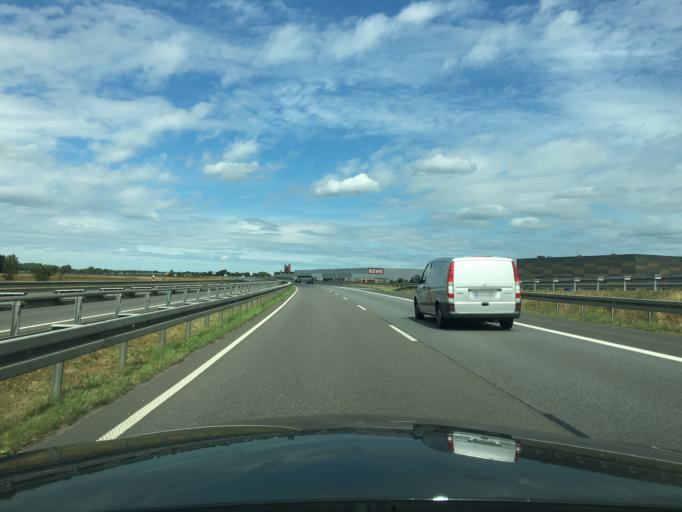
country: DE
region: Brandenburg
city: Leegebruch
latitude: 52.7213
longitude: 13.2179
